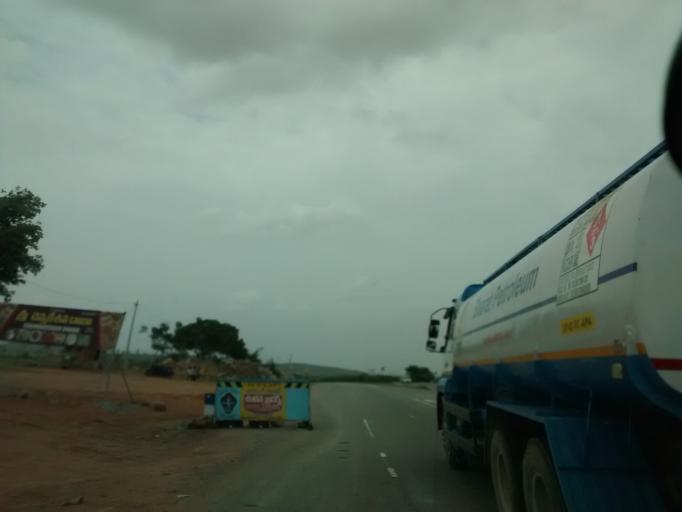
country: IN
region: Andhra Pradesh
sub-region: Kurnool
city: Ramapuram
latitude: 15.2534
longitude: 77.7498
